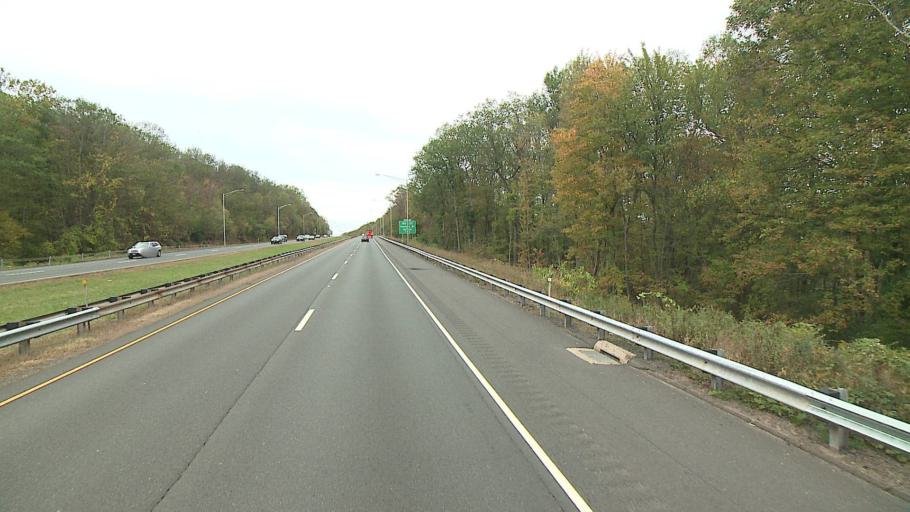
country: US
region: Connecticut
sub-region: Middlesex County
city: Higganum
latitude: 41.5193
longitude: -72.6040
